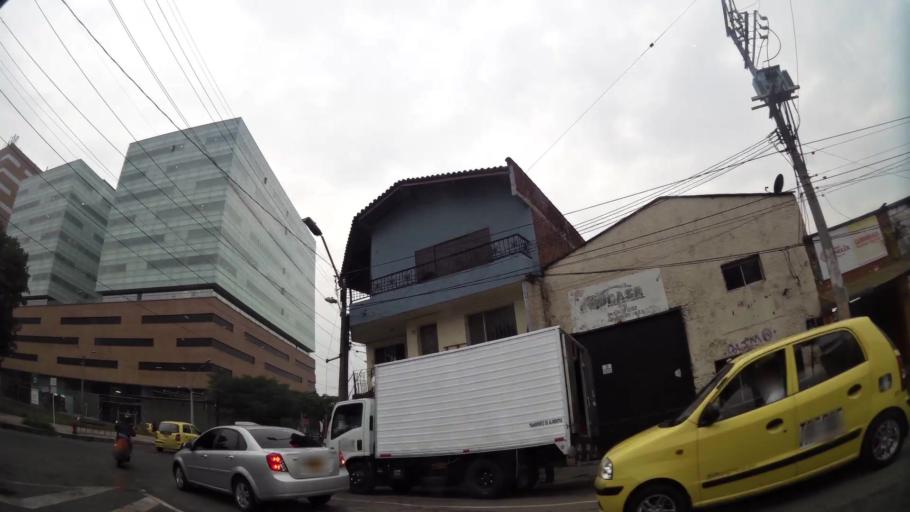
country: CO
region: Antioquia
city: Medellin
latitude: 6.2258
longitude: -75.5739
